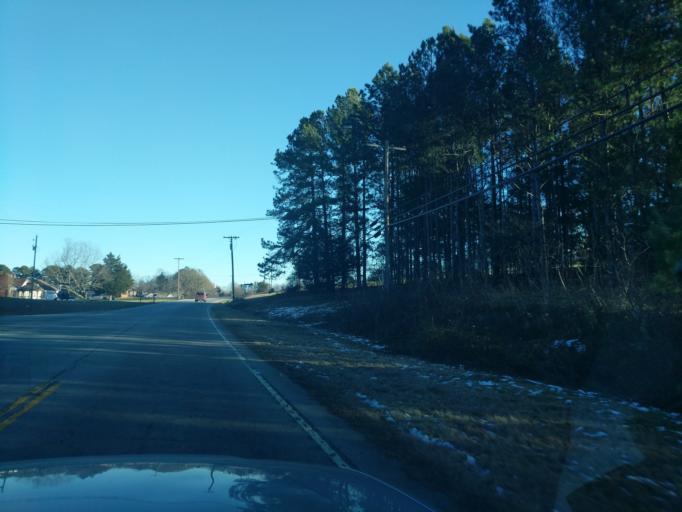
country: US
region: South Carolina
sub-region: Oconee County
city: Westminster
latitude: 34.6807
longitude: -83.1198
